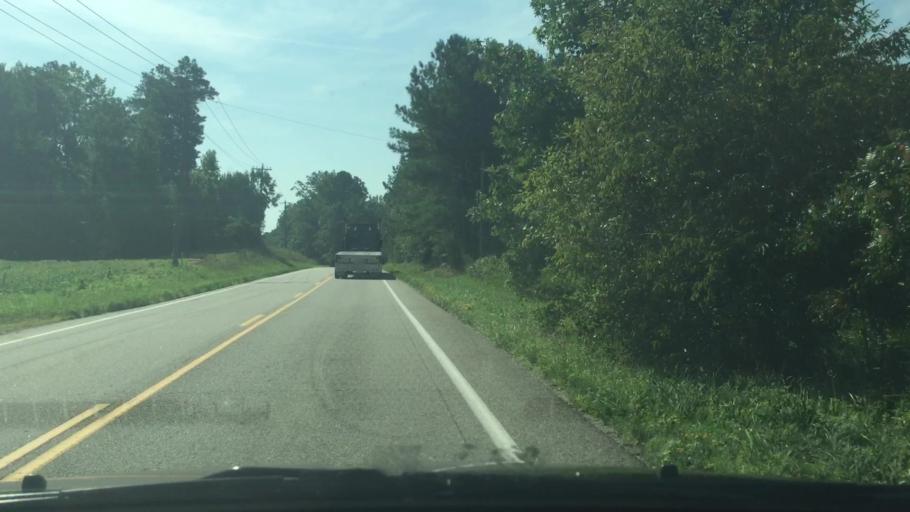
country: US
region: Virginia
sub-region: Sussex County
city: Sussex
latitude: 37.0576
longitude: -77.3273
